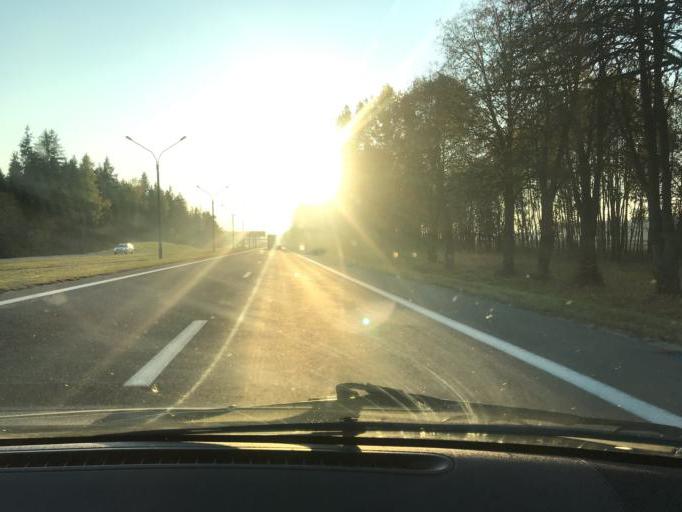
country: BY
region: Minsk
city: Korolev Stan
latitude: 54.0017
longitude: 27.8342
